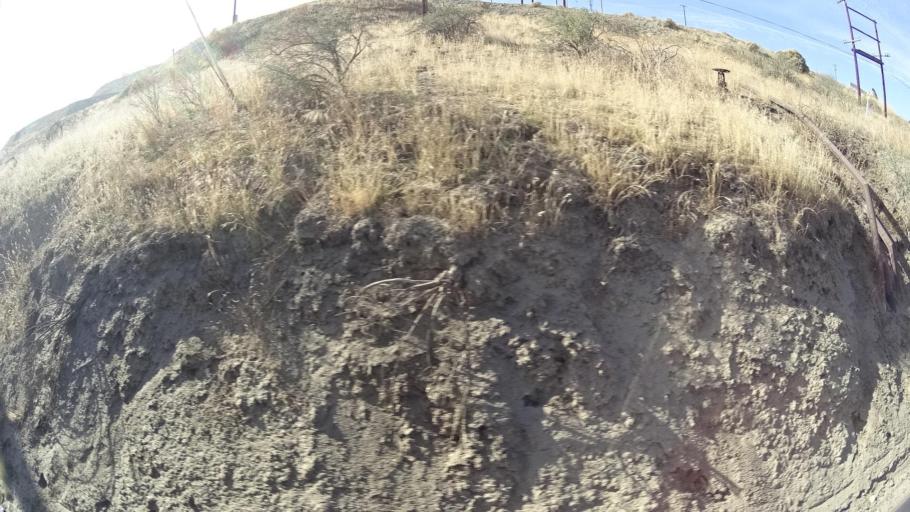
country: US
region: California
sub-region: Kern County
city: Oildale
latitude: 35.5861
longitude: -118.9595
